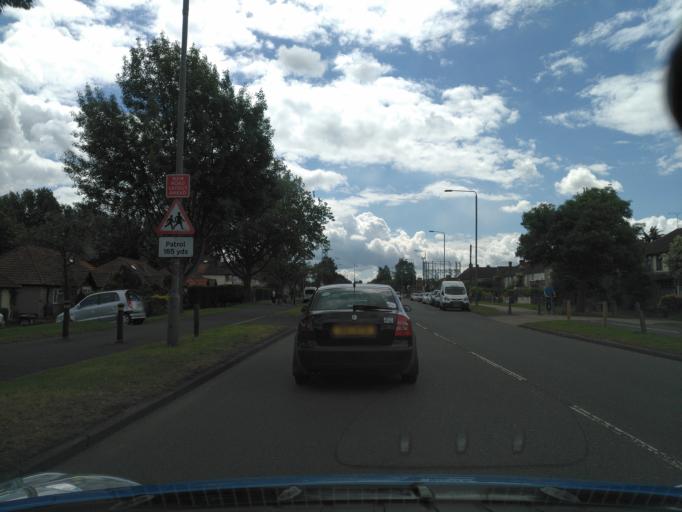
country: GB
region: England
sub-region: Greater London
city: Sidcup
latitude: 51.4039
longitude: 0.1132
